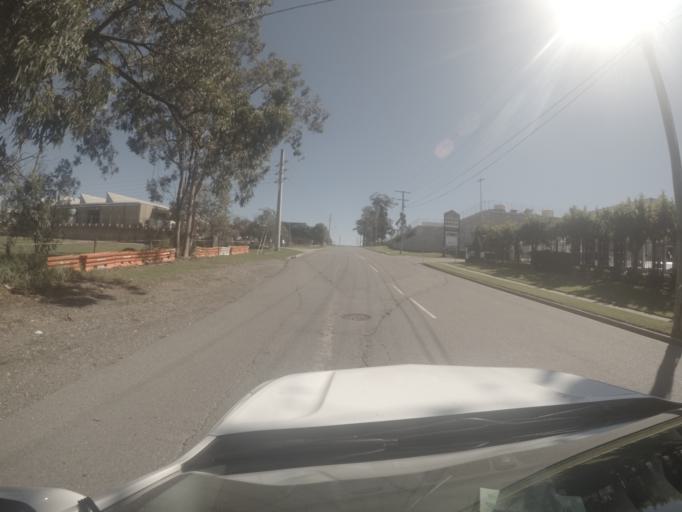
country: AU
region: Queensland
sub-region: Brisbane
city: Richlands
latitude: -27.5773
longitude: 152.9581
